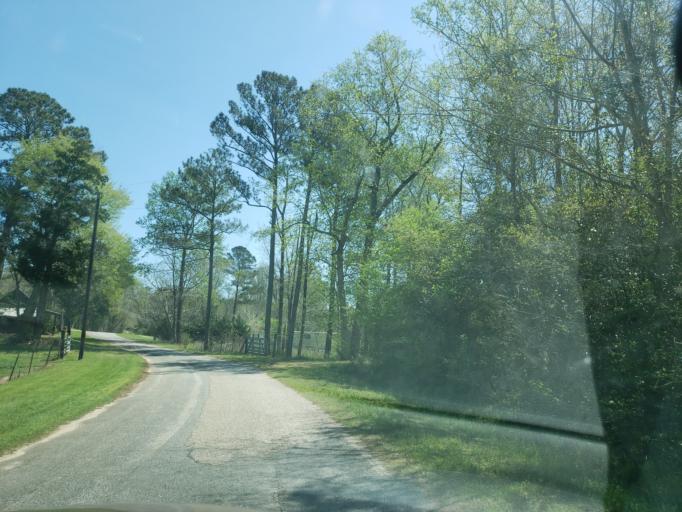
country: US
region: Alabama
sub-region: Elmore County
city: Tallassee
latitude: 32.6664
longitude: -85.8519
